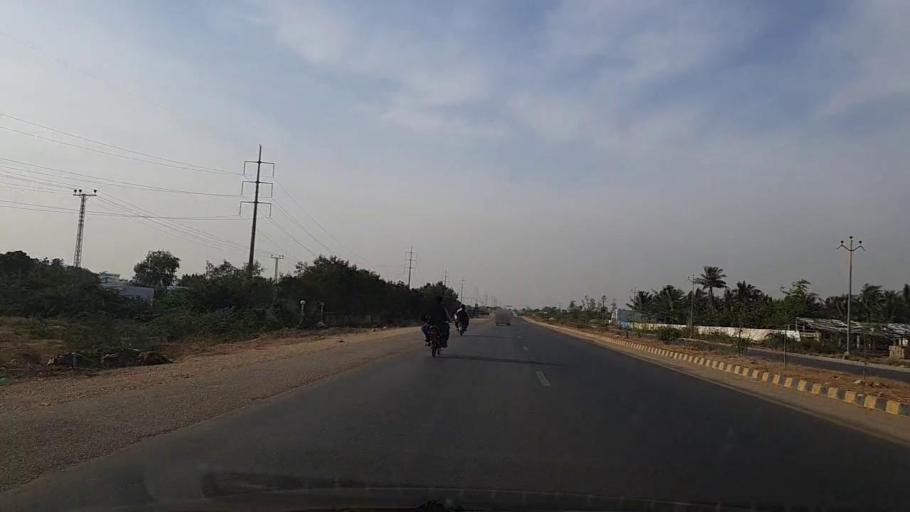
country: PK
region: Sindh
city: Gharo
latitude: 24.7570
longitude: 67.5620
